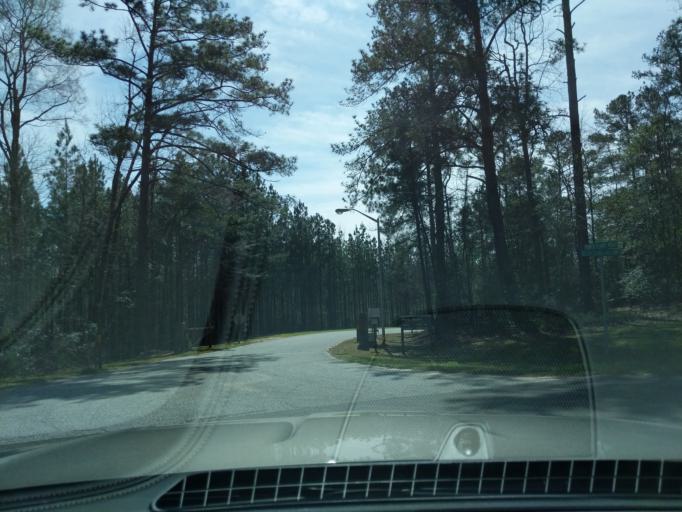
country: US
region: Georgia
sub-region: Columbia County
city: Evans
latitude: 33.6637
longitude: -82.1878
